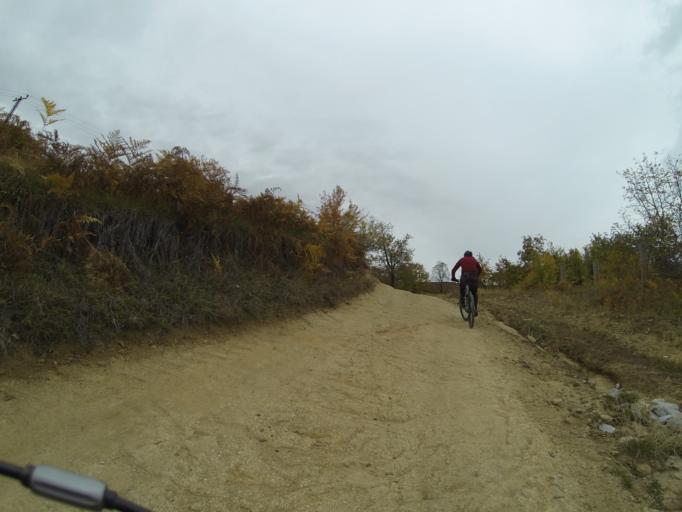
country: RO
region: Gorj
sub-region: Comuna Pades
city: Closani
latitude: 45.1112
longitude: 22.8479
